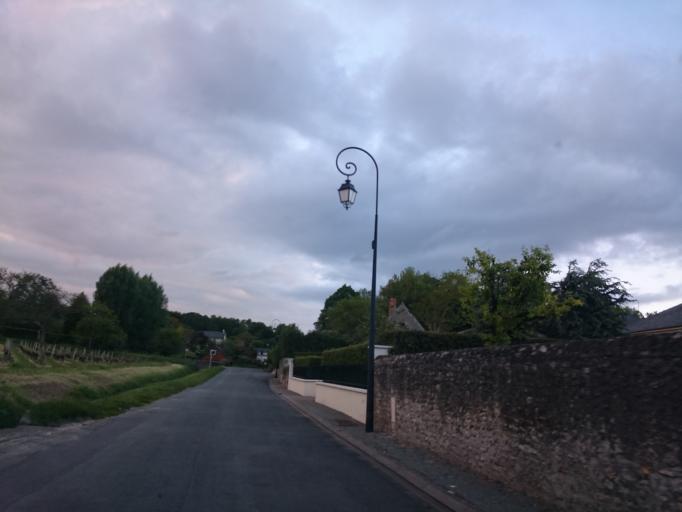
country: FR
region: Centre
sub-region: Departement d'Indre-et-Loire
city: Civray-de-Touraine
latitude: 47.3331
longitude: 1.0663
